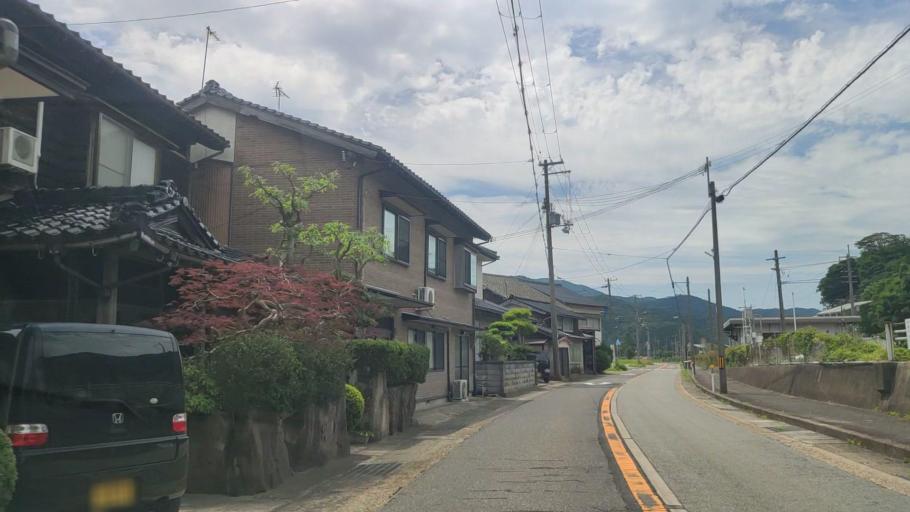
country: JP
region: Hyogo
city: Toyooka
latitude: 35.6495
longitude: 134.7572
